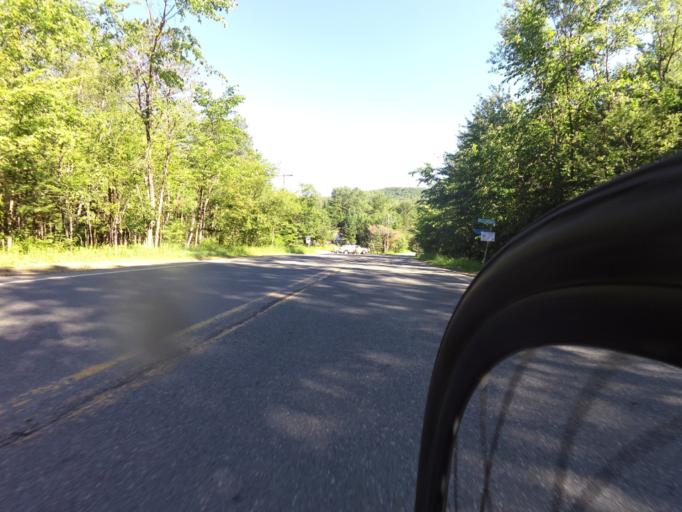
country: CA
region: Quebec
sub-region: Laurentides
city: Brownsburg-Chatham
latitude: 45.8799
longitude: -74.5679
